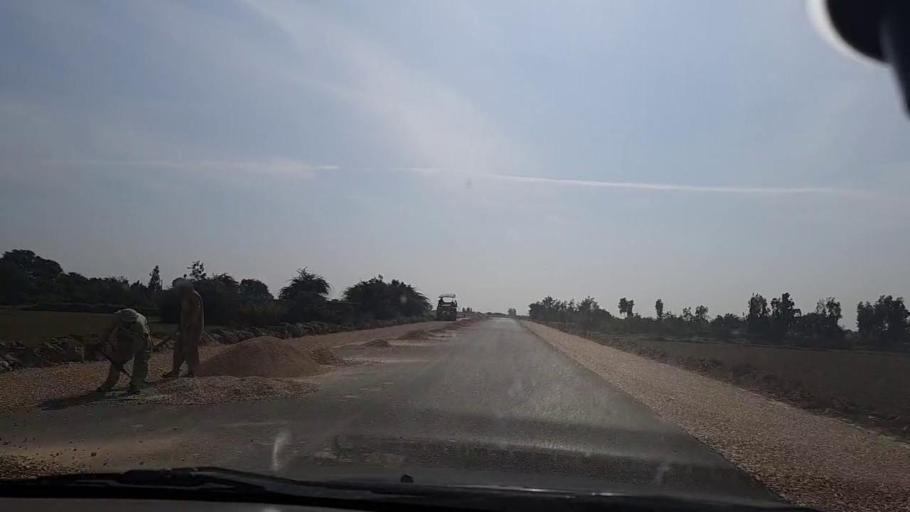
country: PK
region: Sindh
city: Mirpur Batoro
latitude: 24.7373
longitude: 68.2741
